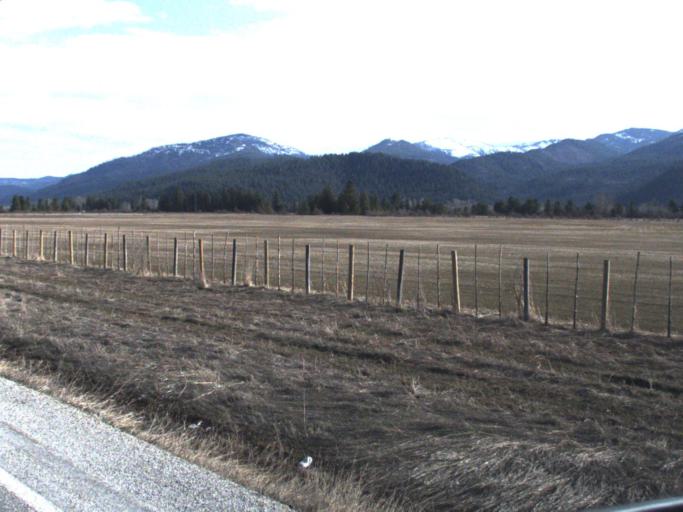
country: US
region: Washington
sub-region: Pend Oreille County
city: Newport
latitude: 48.3649
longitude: -117.3047
